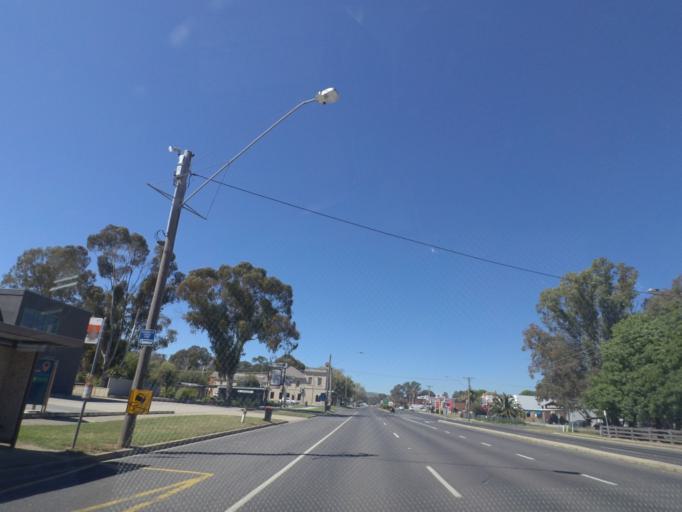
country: AU
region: Victoria
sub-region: Murrindindi
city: Kinglake West
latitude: -37.0209
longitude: 145.1258
